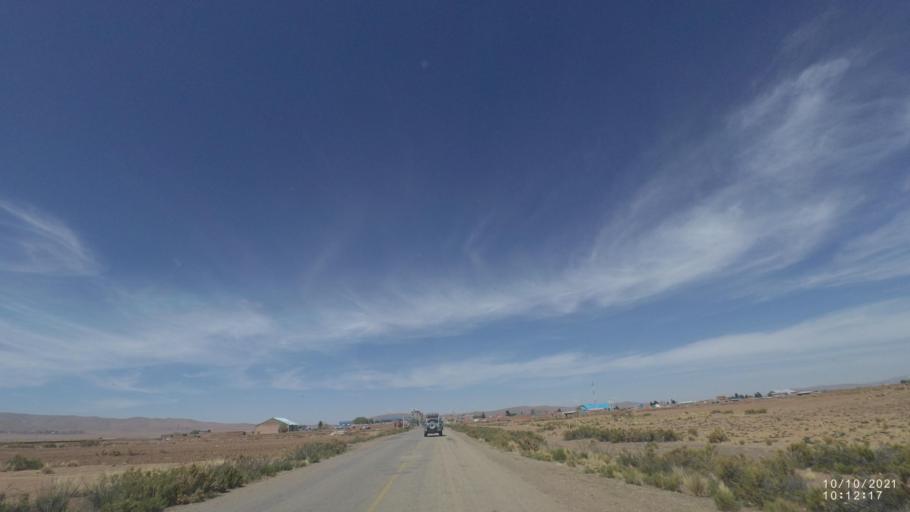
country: BO
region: La Paz
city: Eucaliptus
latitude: -17.4334
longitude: -67.5134
